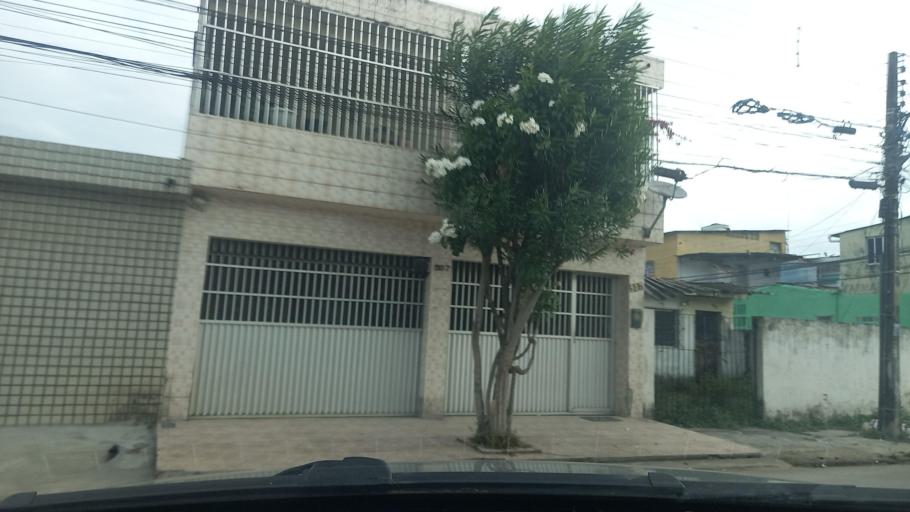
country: BR
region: Pernambuco
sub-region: Recife
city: Recife
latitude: -8.1160
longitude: -34.9213
